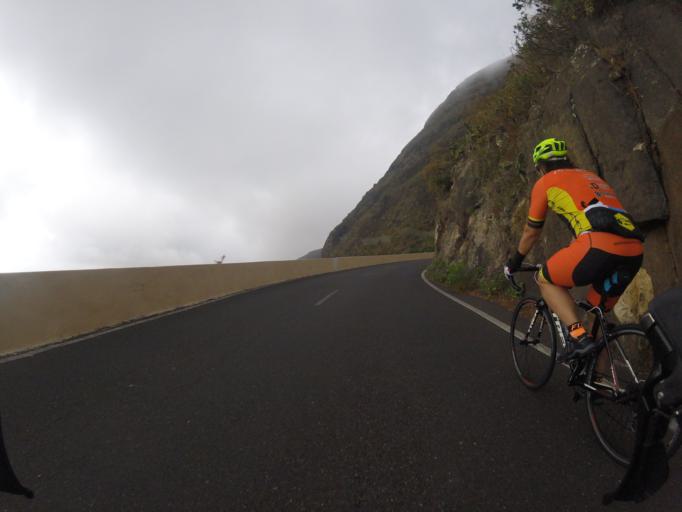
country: ES
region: Canary Islands
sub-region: Provincia de Santa Cruz de Tenerife
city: Guimar
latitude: 28.2959
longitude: -16.4131
